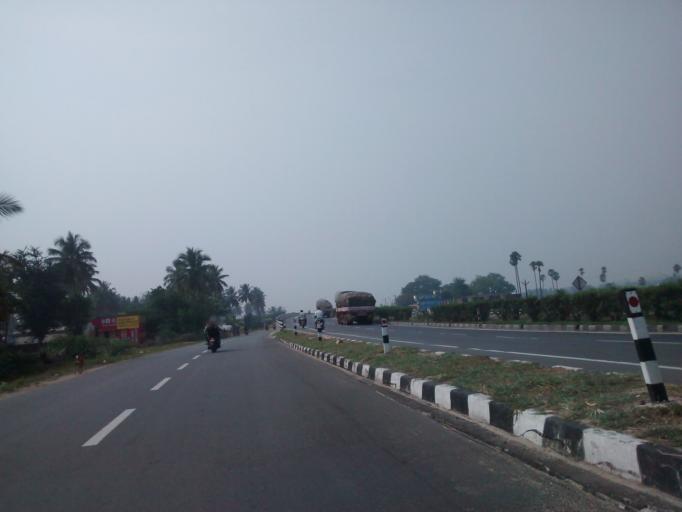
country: IN
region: Tamil Nadu
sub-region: Krishnagiri
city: Krishnagiri
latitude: 12.4850
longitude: 78.2178
